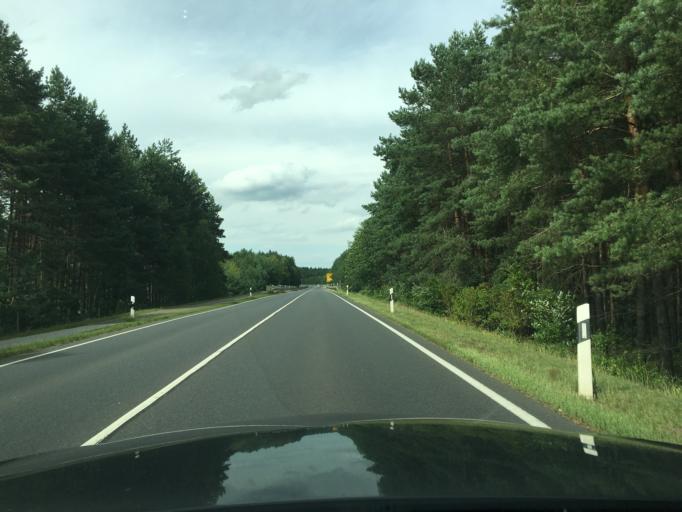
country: DE
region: Mecklenburg-Vorpommern
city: Neustrelitz
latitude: 53.3640
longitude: 13.0919
